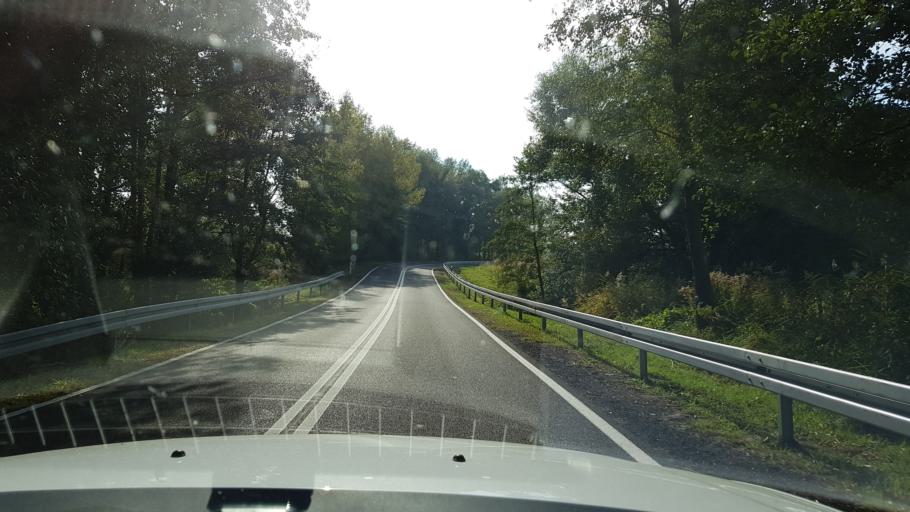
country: PL
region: West Pomeranian Voivodeship
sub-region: Powiat gryfinski
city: Chojna
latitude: 52.9598
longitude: 14.4606
